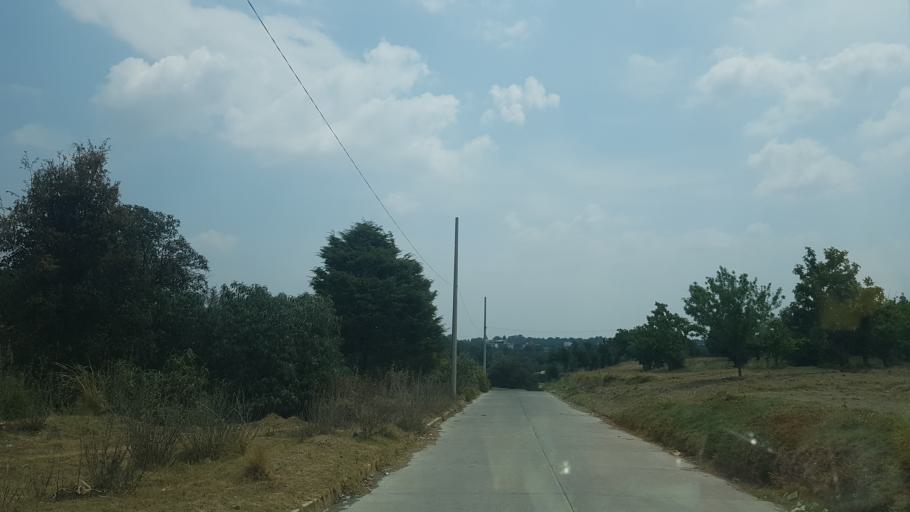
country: MX
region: Puebla
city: Domingo Arenas
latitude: 19.1381
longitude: -98.4788
